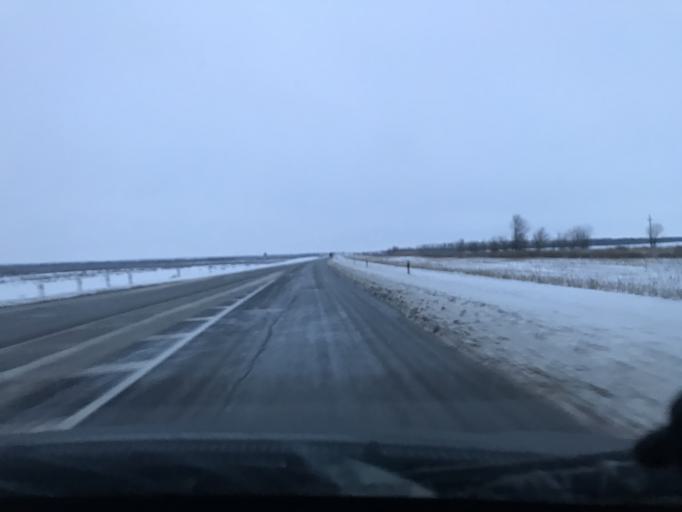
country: RU
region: Rostov
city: Letnik
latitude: 45.9699
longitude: 41.2588
